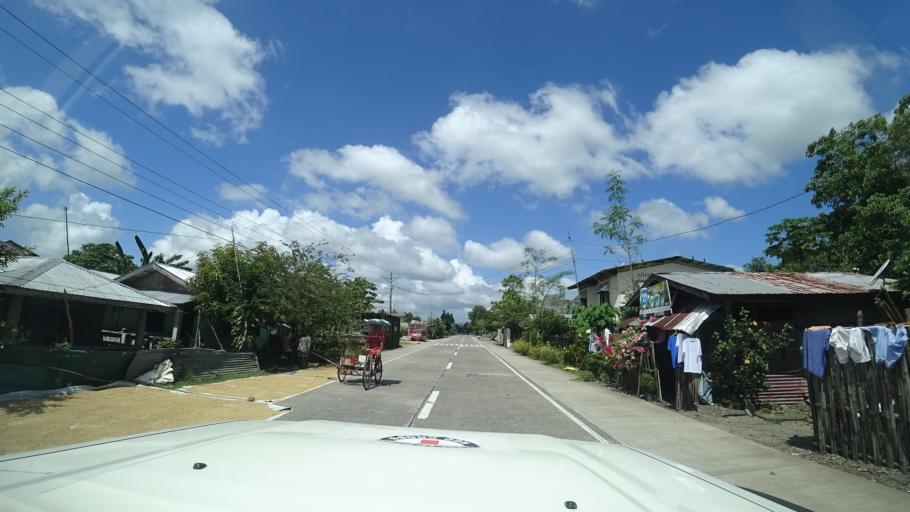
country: PH
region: Eastern Visayas
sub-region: Province of Leyte
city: Mayorga
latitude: 10.9051
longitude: 125.0041
